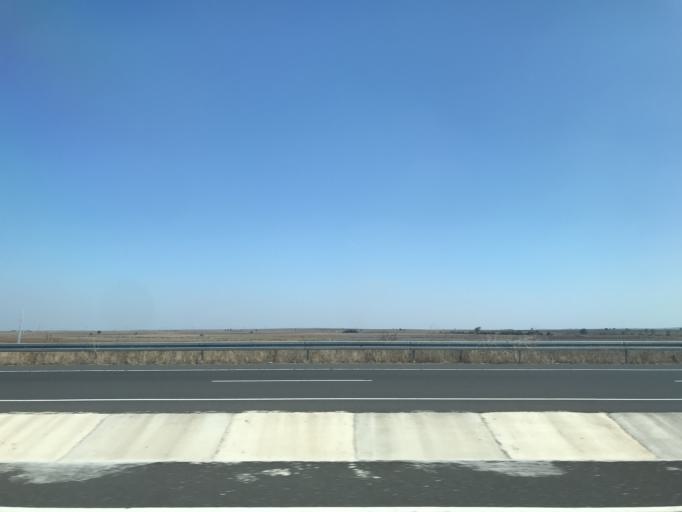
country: TR
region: Tekirdag
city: Muratli
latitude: 41.1876
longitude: 27.5396
